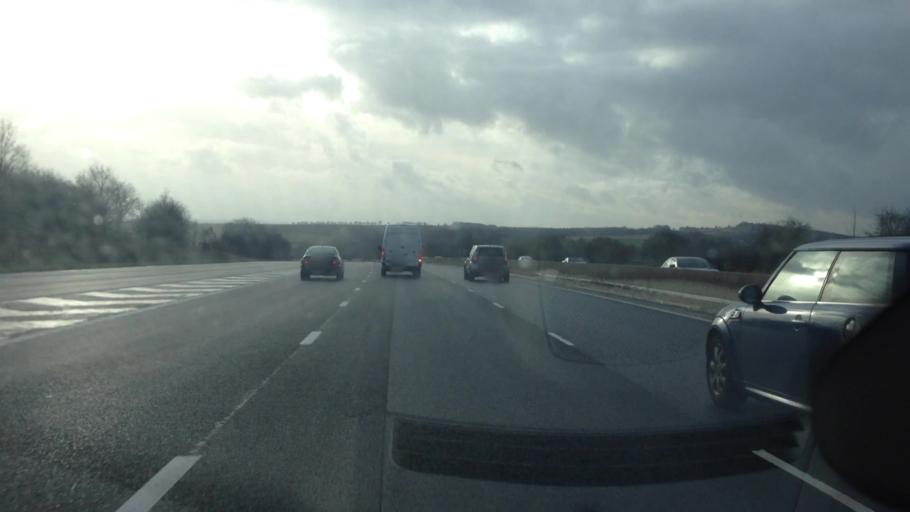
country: GB
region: England
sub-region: City and Borough of Wakefield
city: Crigglestone
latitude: 53.6181
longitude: -1.5508
